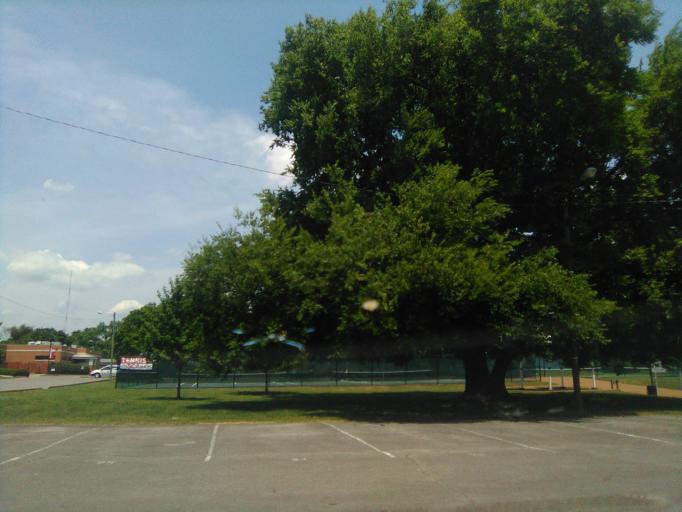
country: US
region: Tennessee
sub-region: Davidson County
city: Belle Meade
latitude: 36.1325
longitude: -86.8409
